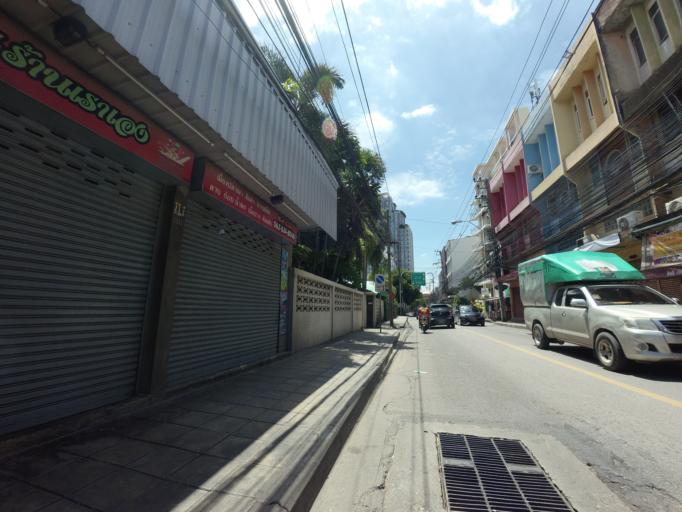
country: TH
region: Bangkok
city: Huai Khwang
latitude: 13.7897
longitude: 100.5716
